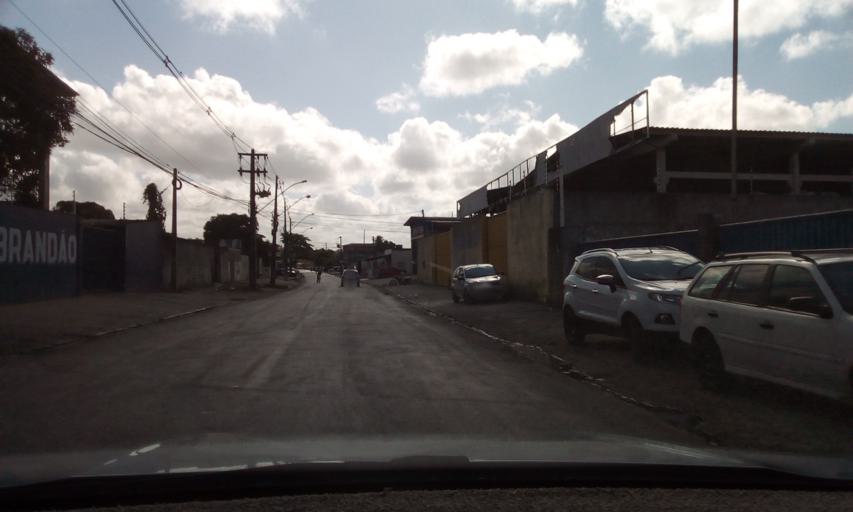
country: BR
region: Paraiba
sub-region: Bayeux
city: Bayeux
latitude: -7.1565
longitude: -34.9036
